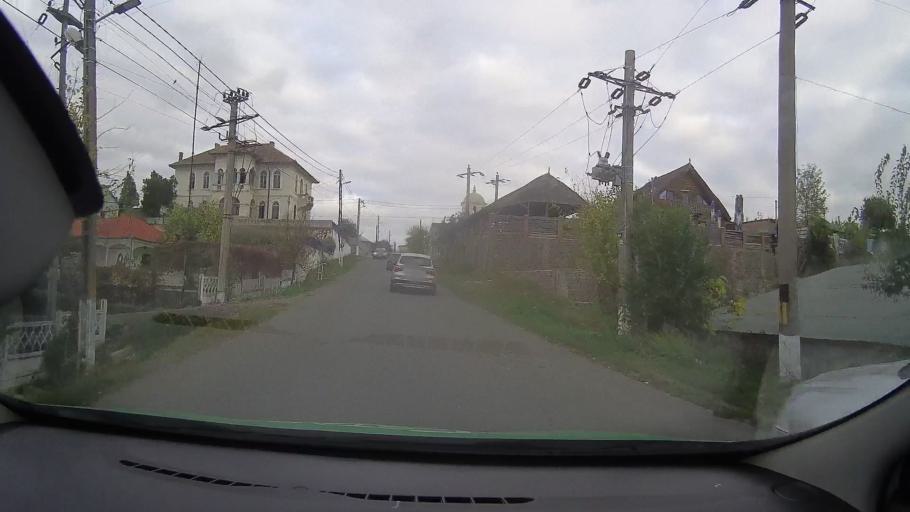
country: RO
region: Tulcea
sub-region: Comuna Jurilovca
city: Jurilovca
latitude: 44.7552
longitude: 28.8759
